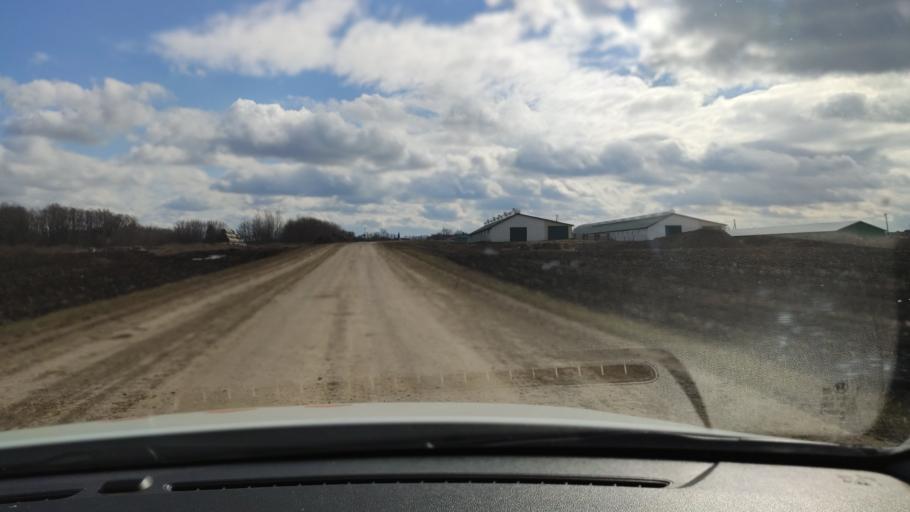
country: RU
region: Tatarstan
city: Vysokaya Gora
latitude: 56.2154
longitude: 49.3128
